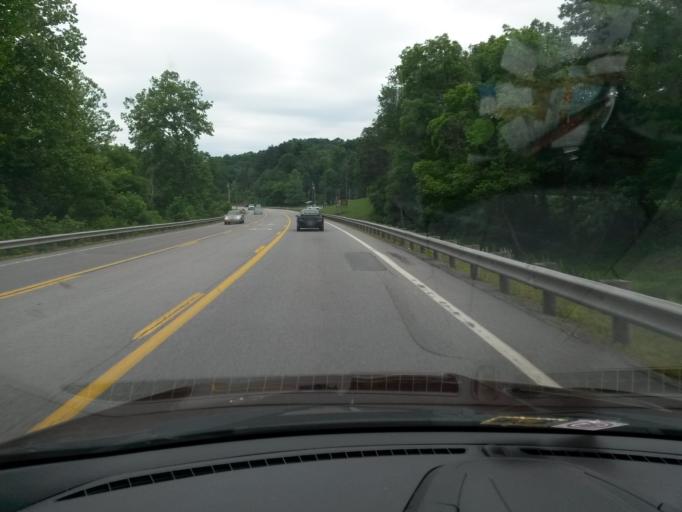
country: US
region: West Virginia
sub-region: Lewis County
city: Weston
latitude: 39.0300
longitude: -80.4355
